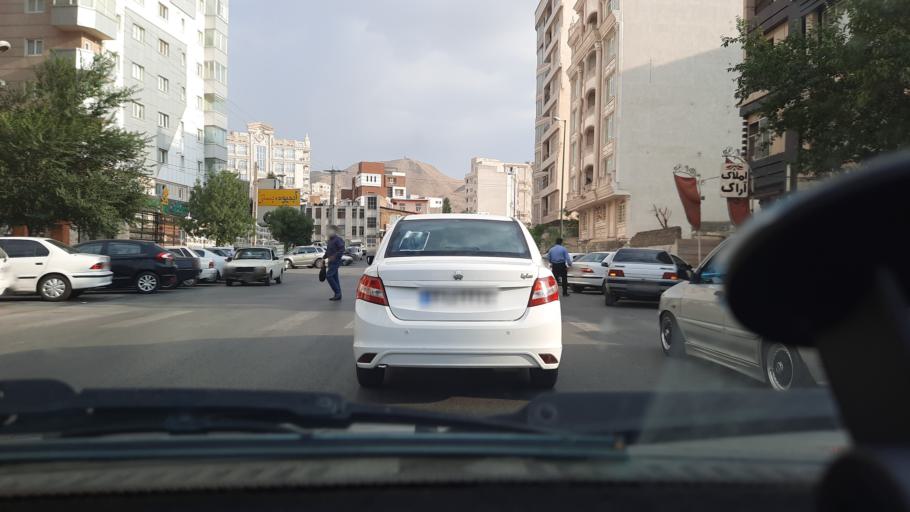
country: IR
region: Markazi
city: Arak
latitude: 34.0769
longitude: 49.6767
